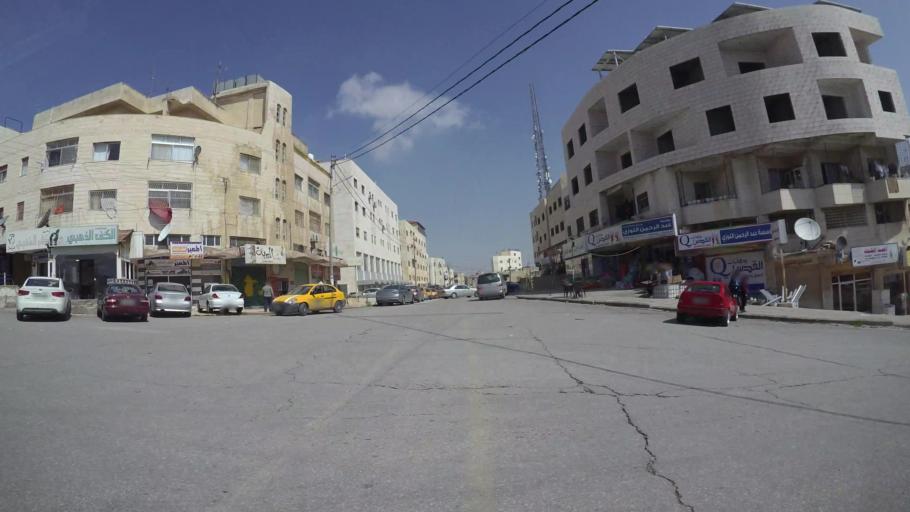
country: JO
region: Amman
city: Al Bunayyat ash Shamaliyah
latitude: 31.9259
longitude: 35.9021
